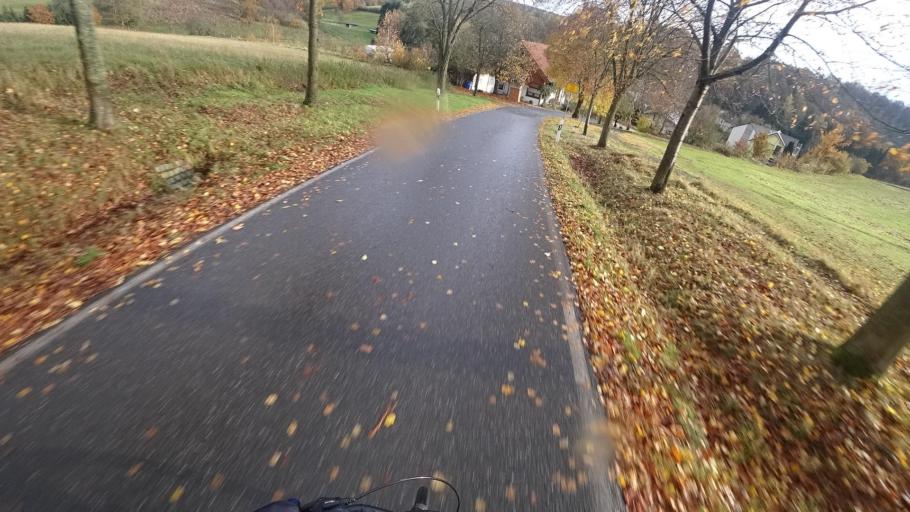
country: DE
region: Rheinland-Pfalz
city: Ney
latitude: 50.1841
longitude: 7.5175
